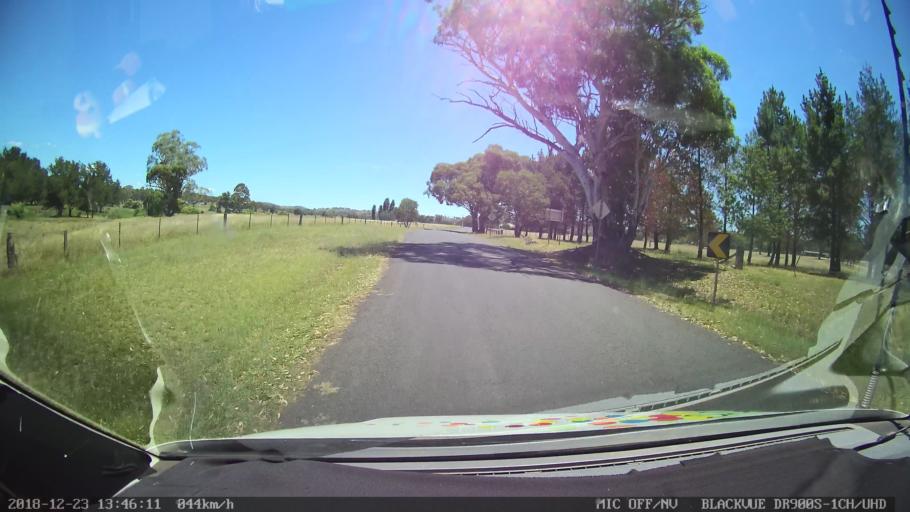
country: AU
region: New South Wales
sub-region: Tamworth Municipality
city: Manilla
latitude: -30.5045
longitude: 151.1210
